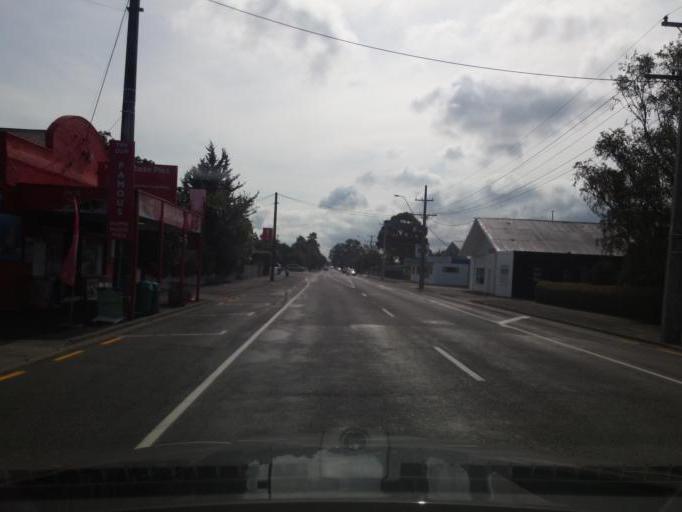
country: NZ
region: Wellington
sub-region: Masterton District
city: Masterton
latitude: -41.0879
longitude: 175.4520
